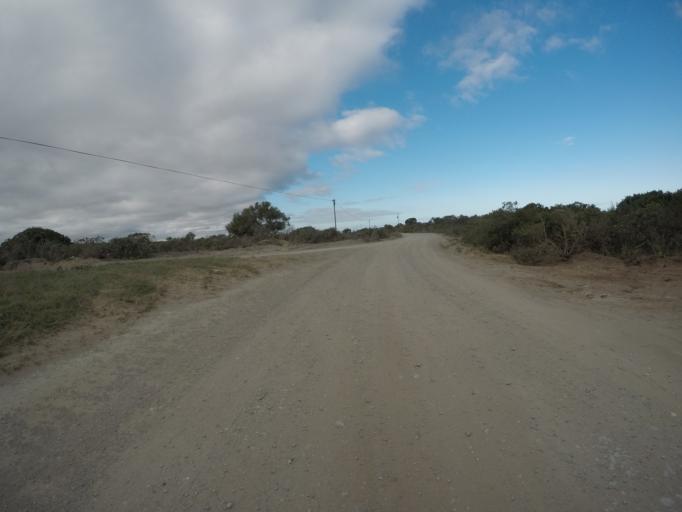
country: ZA
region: Western Cape
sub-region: Eden District Municipality
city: Riversdale
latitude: -34.4210
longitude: 21.3319
